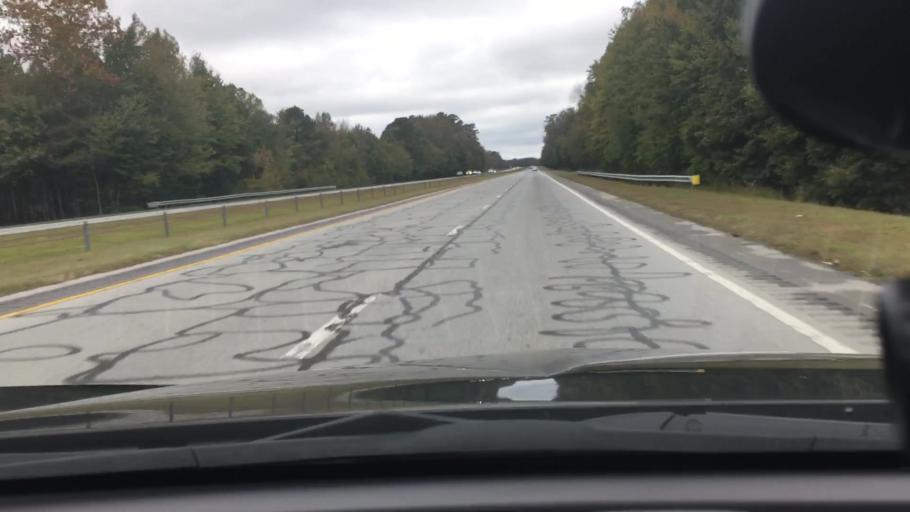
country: US
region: North Carolina
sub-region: Pitt County
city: Farmville
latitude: 35.6094
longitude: -77.5748
